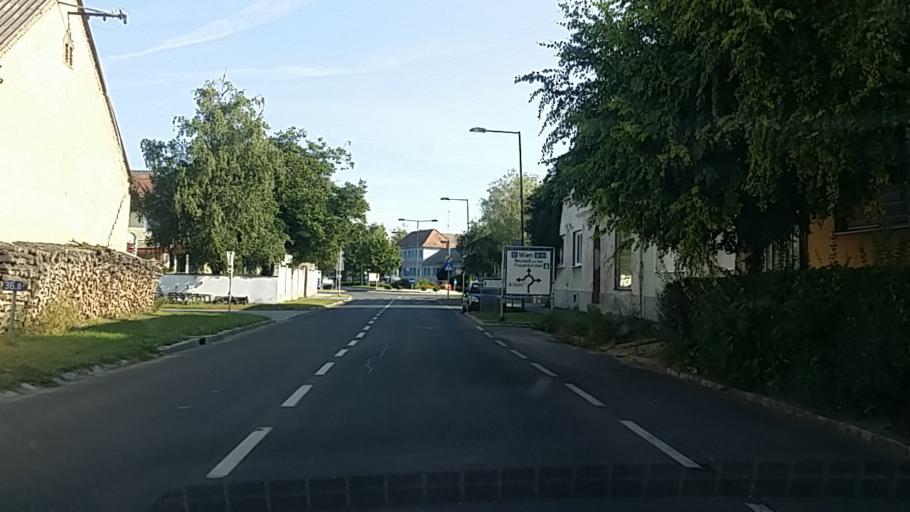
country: AT
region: Burgenland
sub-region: Politischer Bezirk Neusiedl am See
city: Pamhagen
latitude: 47.6983
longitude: 16.9104
